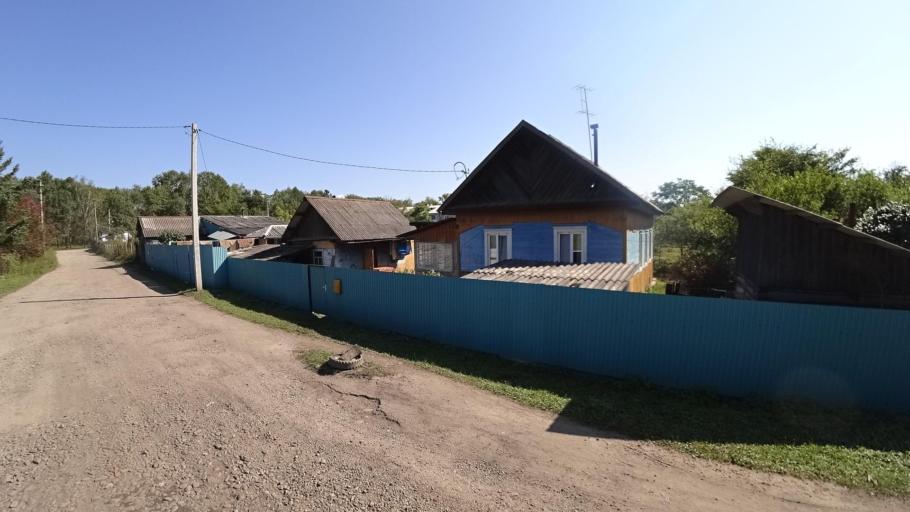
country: RU
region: Jewish Autonomous Oblast
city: Bira
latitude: 48.9980
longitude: 132.4556
